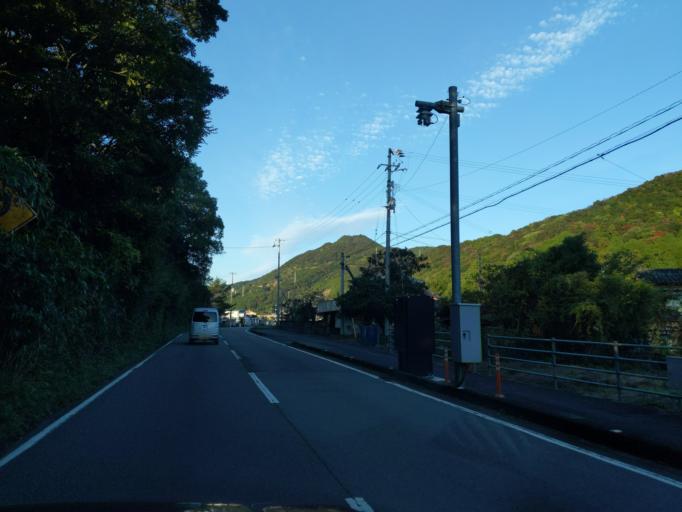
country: JP
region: Kochi
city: Muroto-misakicho
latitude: 33.5825
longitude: 134.3275
